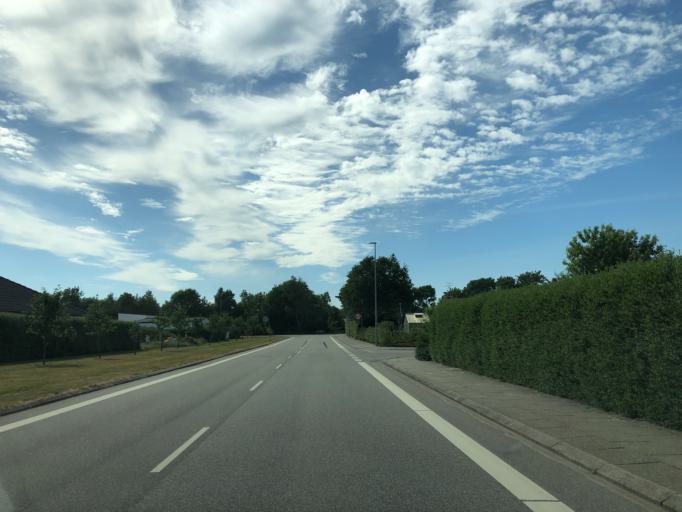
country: DK
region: Central Jutland
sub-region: Herning Kommune
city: Snejbjerg
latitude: 56.1266
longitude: 8.8896
